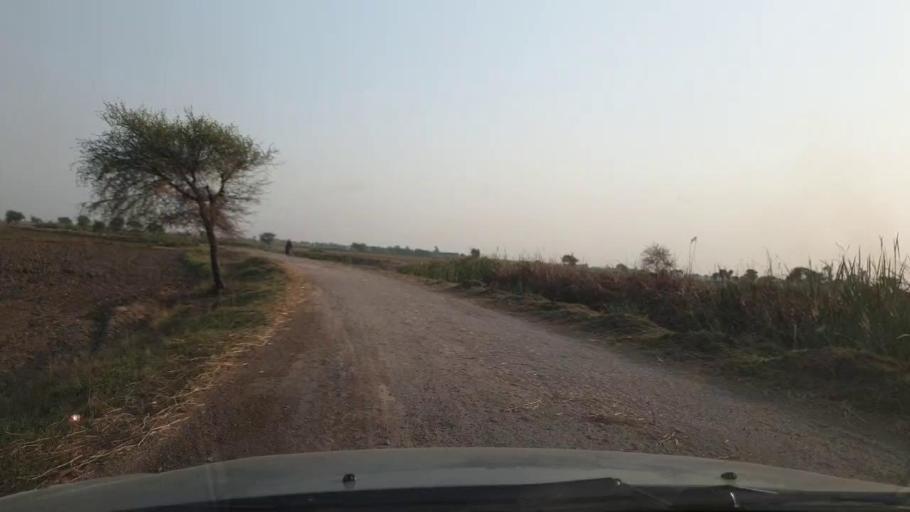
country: PK
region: Sindh
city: Tando Muhammad Khan
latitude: 25.0279
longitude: 68.4370
